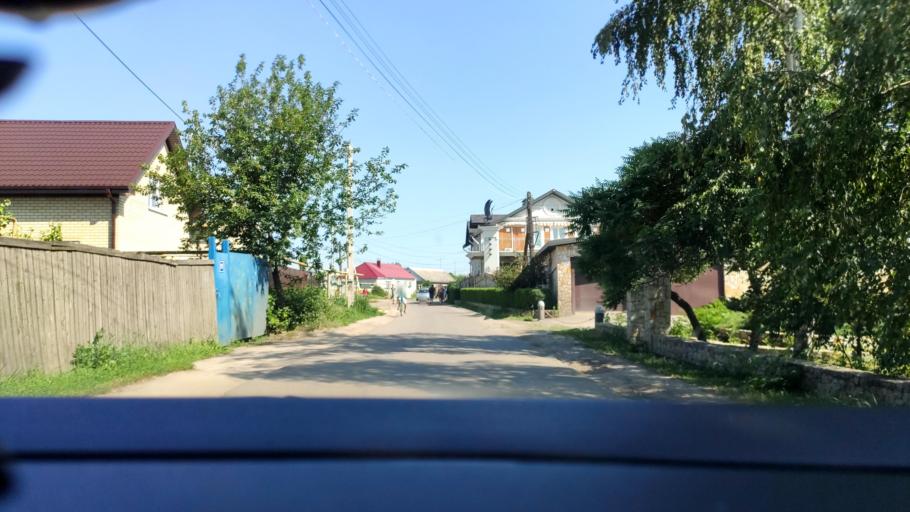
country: RU
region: Voronezj
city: Novaya Usman'
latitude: 51.6389
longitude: 39.4106
